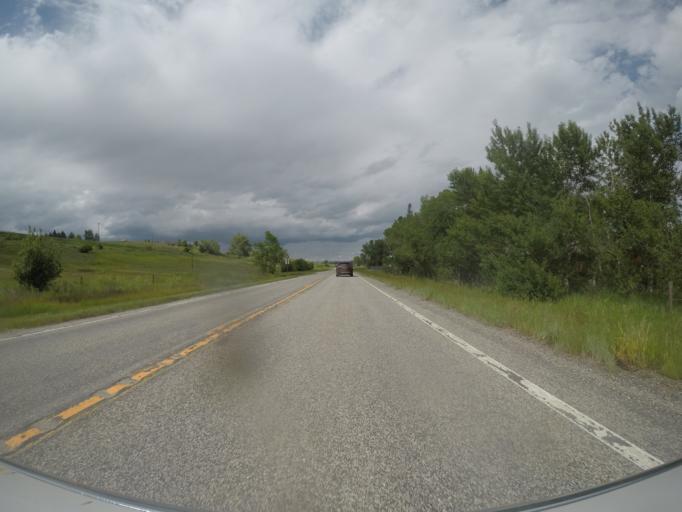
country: US
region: Montana
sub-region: Sweet Grass County
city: Big Timber
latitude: 45.8211
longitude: -109.9541
